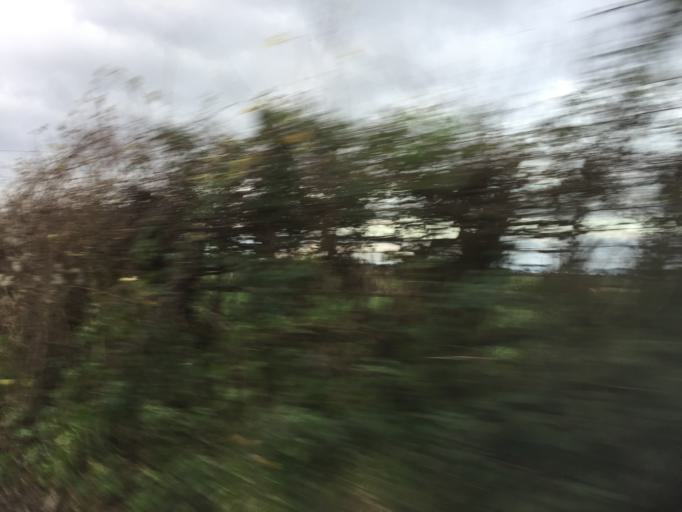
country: GB
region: Wales
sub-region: Monmouthshire
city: Caldicot
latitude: 51.6015
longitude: -2.7100
